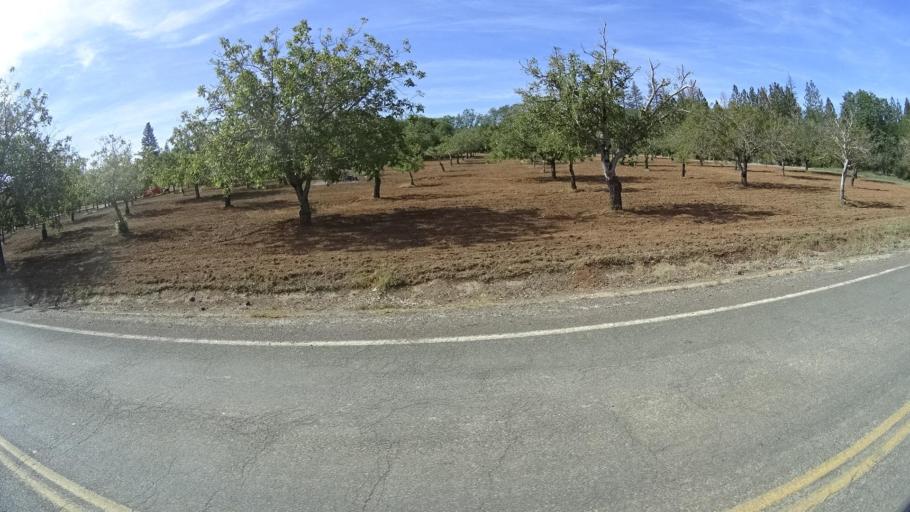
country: US
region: California
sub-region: Lake County
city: Soda Bay
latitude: 38.9124
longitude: -122.7600
